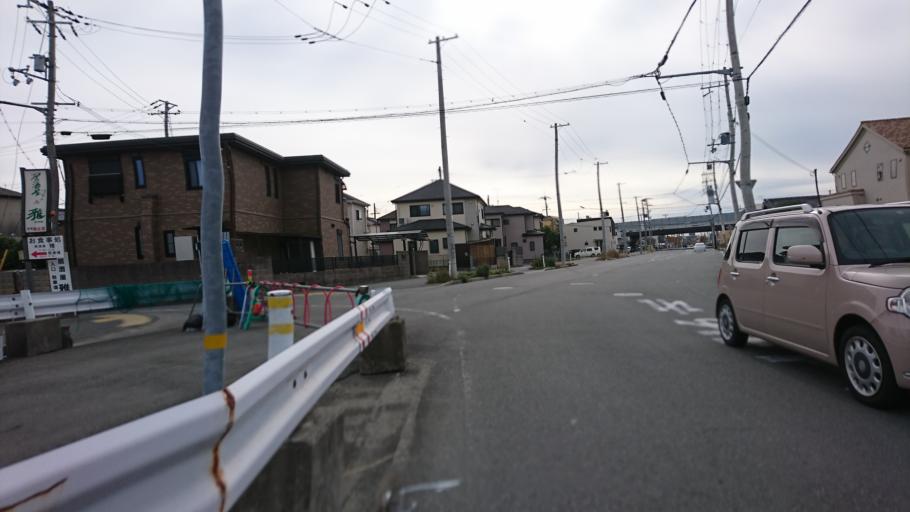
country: JP
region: Hyogo
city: Kakogawacho-honmachi
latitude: 34.7680
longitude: 134.8504
